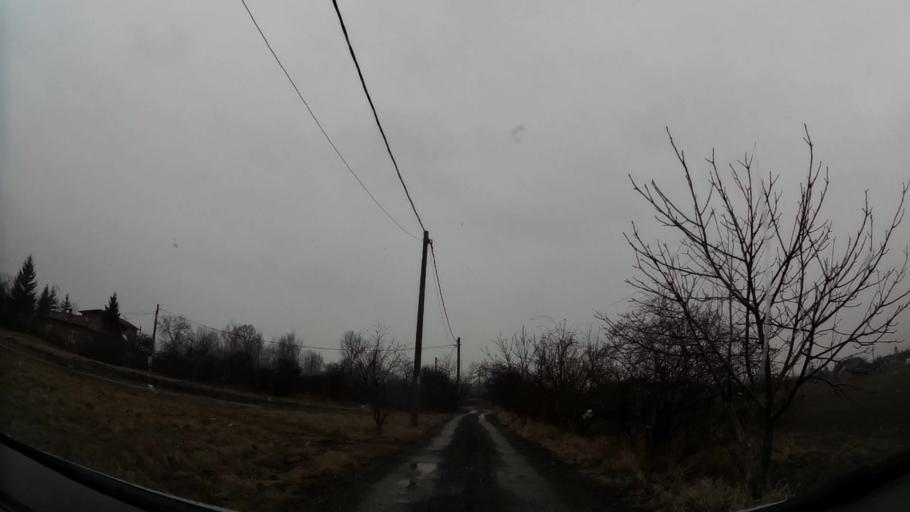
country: BG
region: Sofia-Capital
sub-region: Stolichna Obshtina
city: Sofia
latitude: 42.6672
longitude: 23.4249
